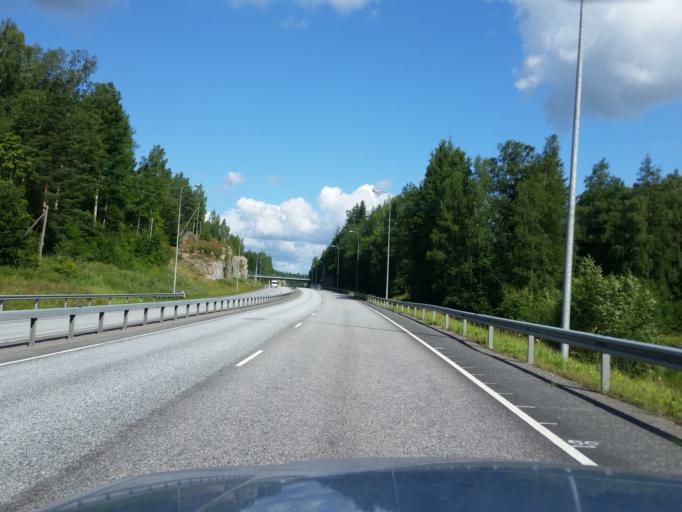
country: FI
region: Uusimaa
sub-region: Helsinki
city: Vihti
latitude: 60.3199
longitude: 24.3434
